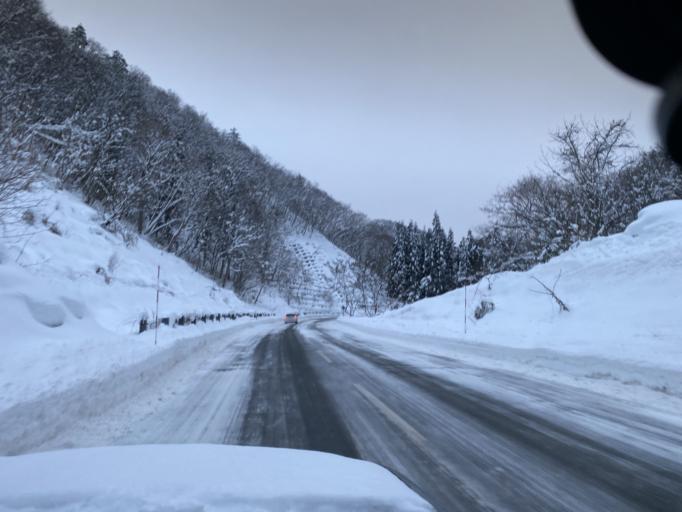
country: JP
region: Nagano
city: Omachi
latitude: 36.5880
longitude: 137.8891
